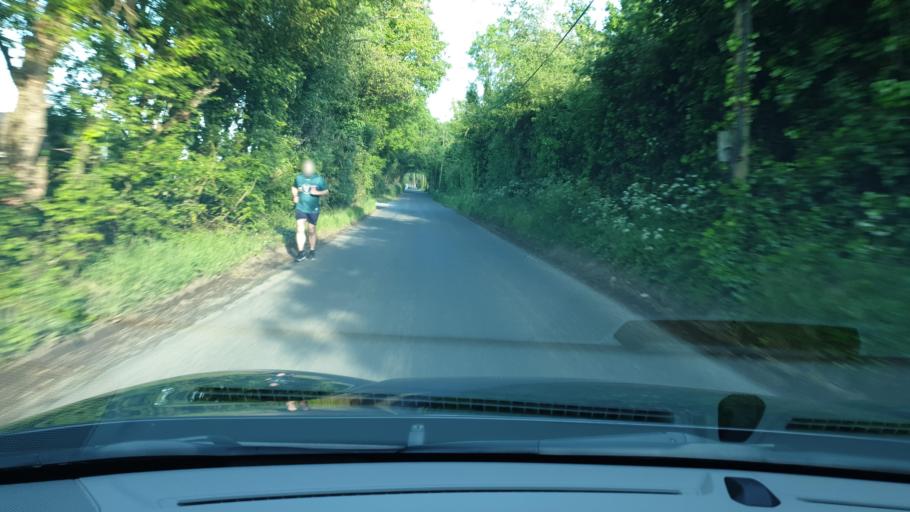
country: IE
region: Leinster
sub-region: An Mhi
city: Ashbourne
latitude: 53.5358
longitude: -6.3211
